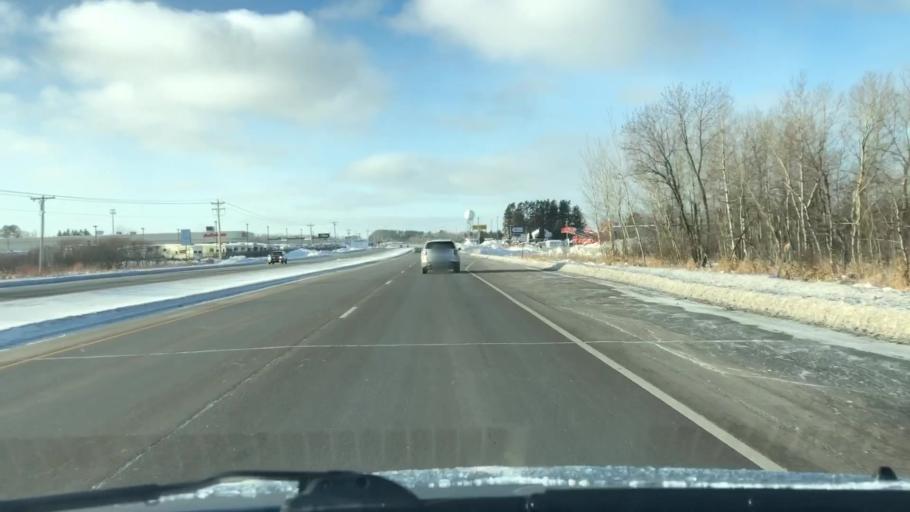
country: US
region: Minnesota
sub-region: Saint Louis County
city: Hermantown
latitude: 46.8306
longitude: -92.2004
